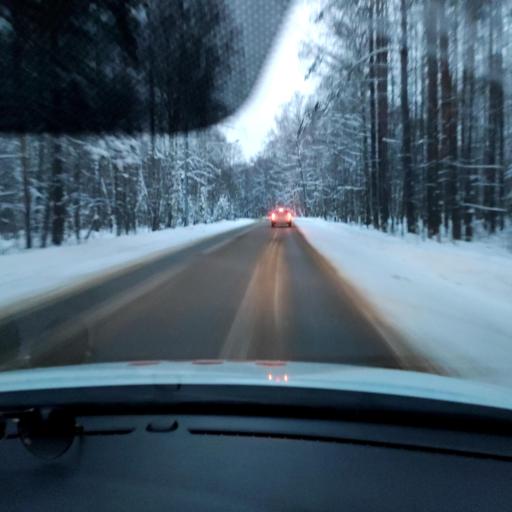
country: RU
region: Tatarstan
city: Vysokaya Gora
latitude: 55.9300
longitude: 49.1607
